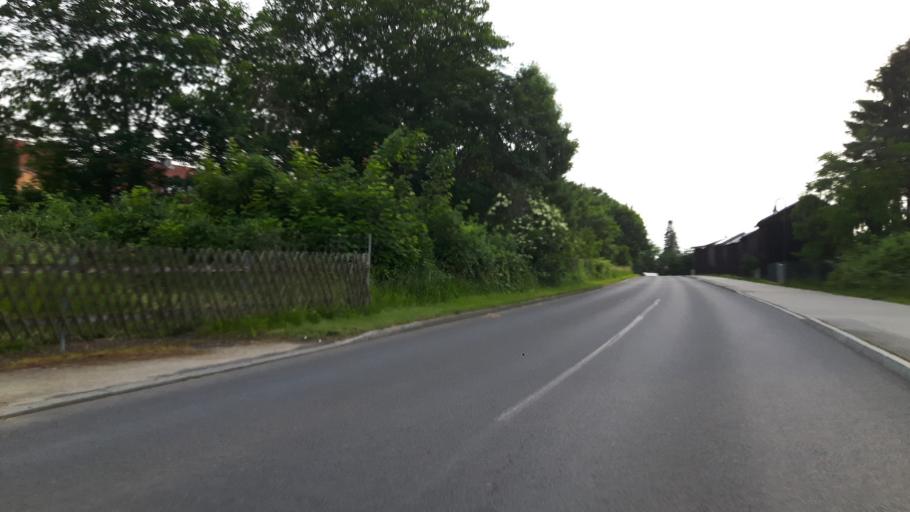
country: DE
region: Brandenburg
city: Gartz
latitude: 53.2109
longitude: 14.3890
